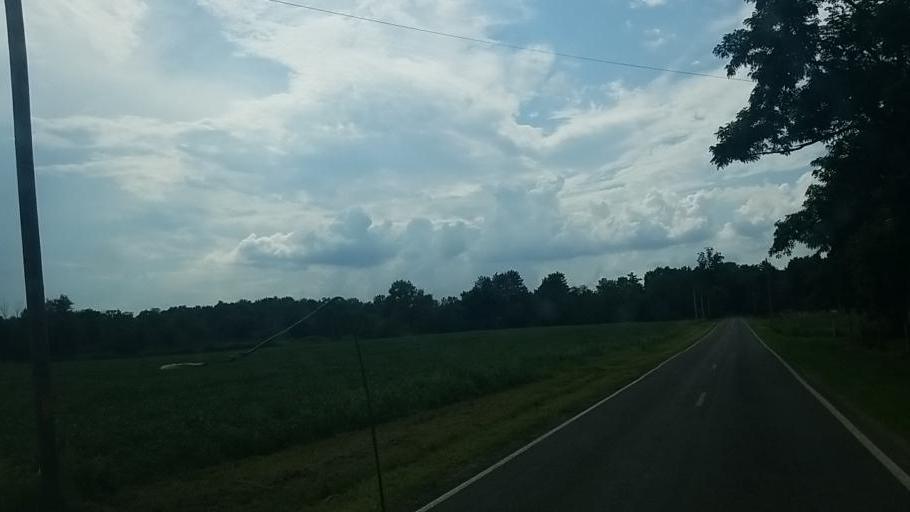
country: US
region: Ohio
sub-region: Wayne County
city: Creston
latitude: 41.0028
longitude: -81.8999
